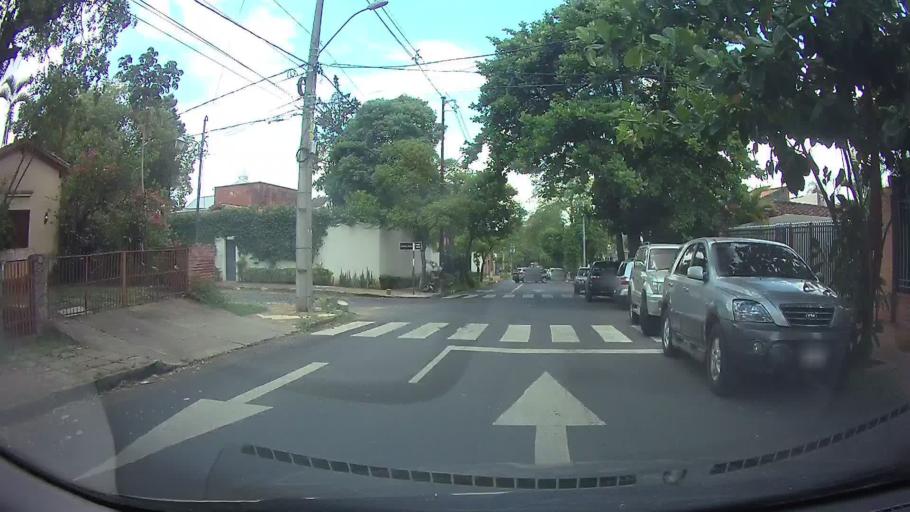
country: PY
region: Asuncion
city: Asuncion
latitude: -25.2955
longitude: -57.5985
